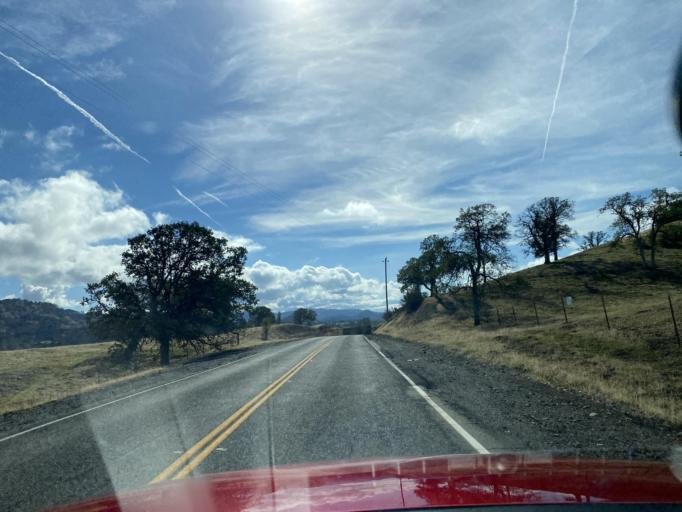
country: US
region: California
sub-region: Glenn County
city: Willows
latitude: 39.4746
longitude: -122.5137
